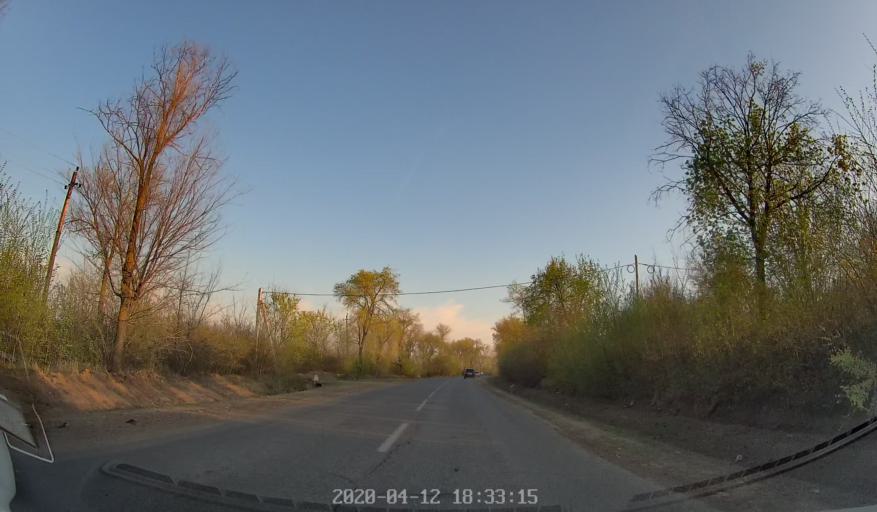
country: MD
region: Chisinau
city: Vadul lui Voda
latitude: 47.1267
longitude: 29.0633
